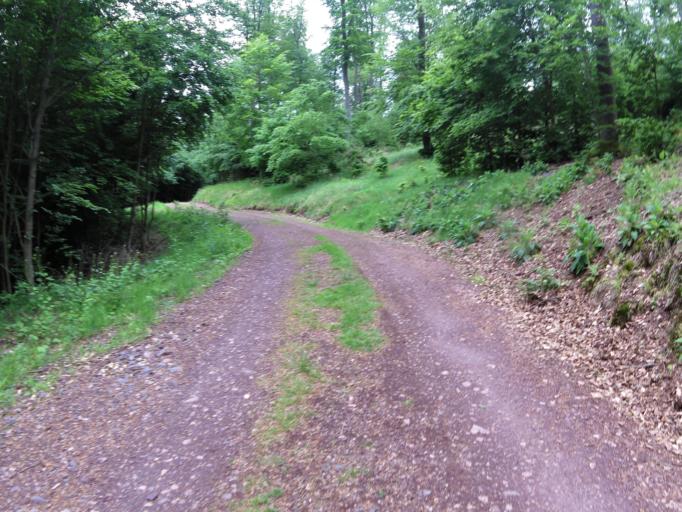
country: DE
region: Thuringia
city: Eisenach
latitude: 50.9443
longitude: 10.3183
